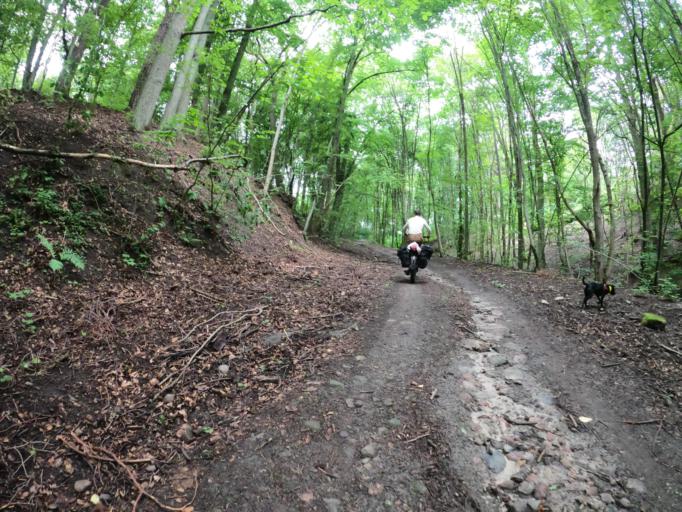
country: PL
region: West Pomeranian Voivodeship
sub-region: Powiat bialogardzki
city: Tychowo
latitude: 53.9781
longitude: 16.3934
